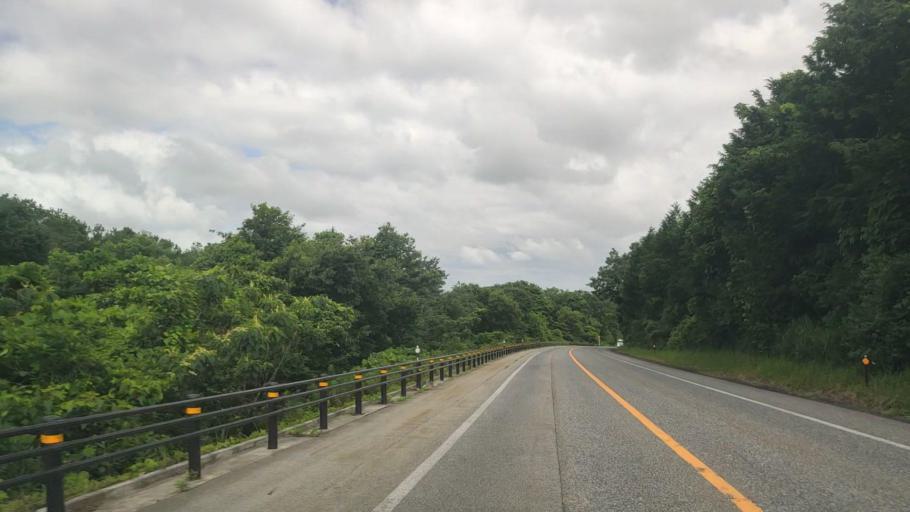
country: JP
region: Tottori
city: Yonago
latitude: 35.4173
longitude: 133.4442
